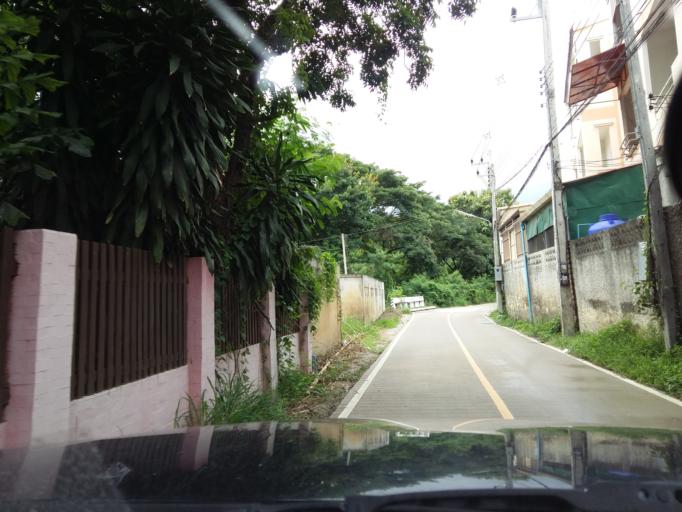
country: TH
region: Chiang Mai
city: Chiang Mai
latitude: 18.7467
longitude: 98.9818
